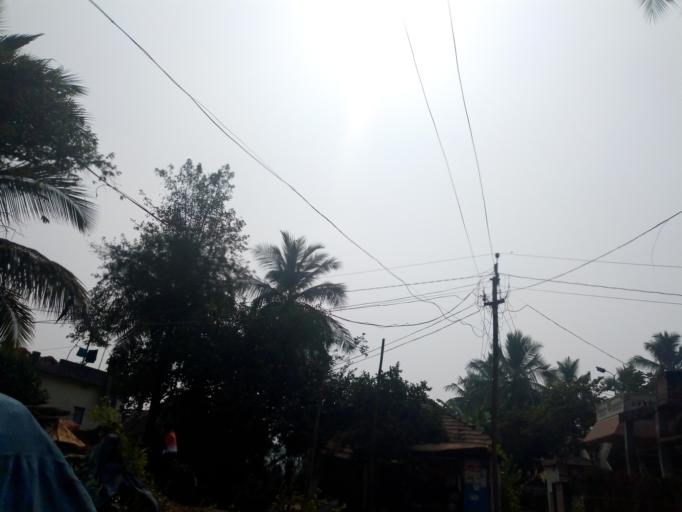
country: IN
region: Andhra Pradesh
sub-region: West Godavari
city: Tadepallegudem
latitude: 16.8622
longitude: 81.3170
